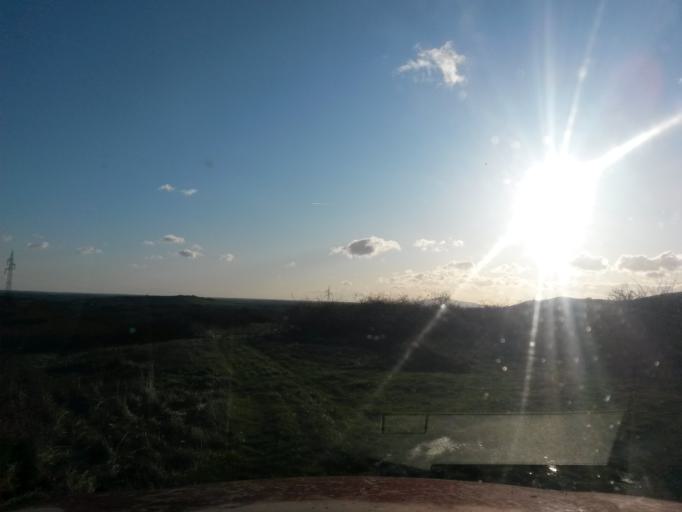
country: HU
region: Borsod-Abauj-Zemplen
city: Sarospatak
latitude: 48.3260
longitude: 21.5382
